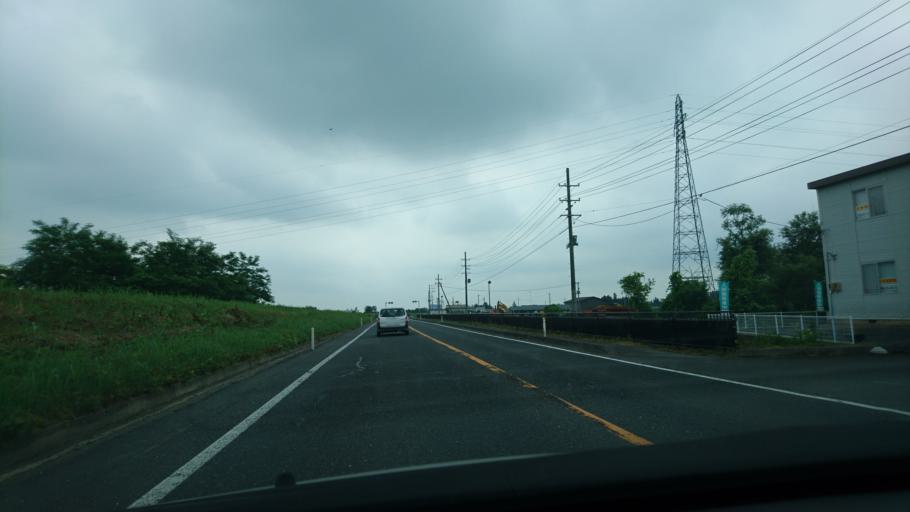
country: JP
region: Miyagi
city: Furukawa
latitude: 38.6202
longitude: 140.9093
